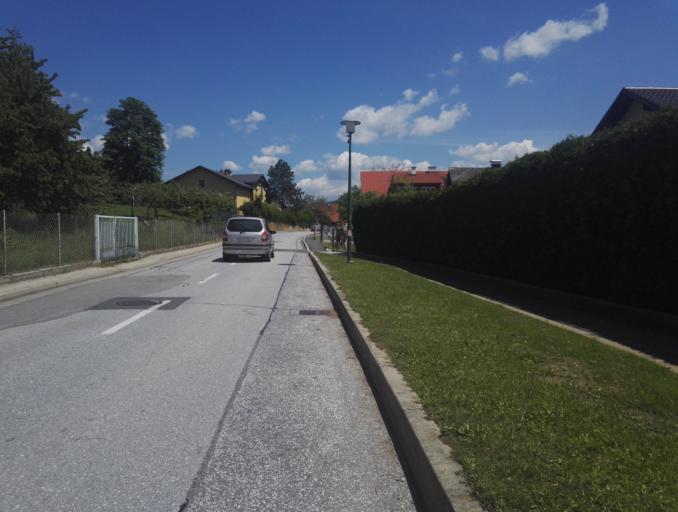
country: AT
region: Styria
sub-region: Politischer Bezirk Graz-Umgebung
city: Deutschfeistritz
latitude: 47.1782
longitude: 15.3219
